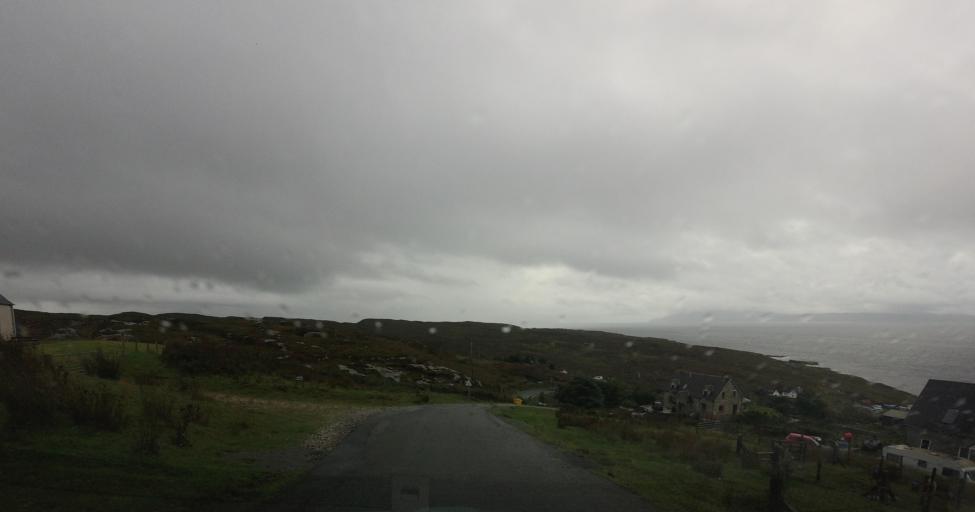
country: GB
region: Scotland
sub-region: Highland
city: Isle of Skye
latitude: 57.1478
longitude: -6.1024
